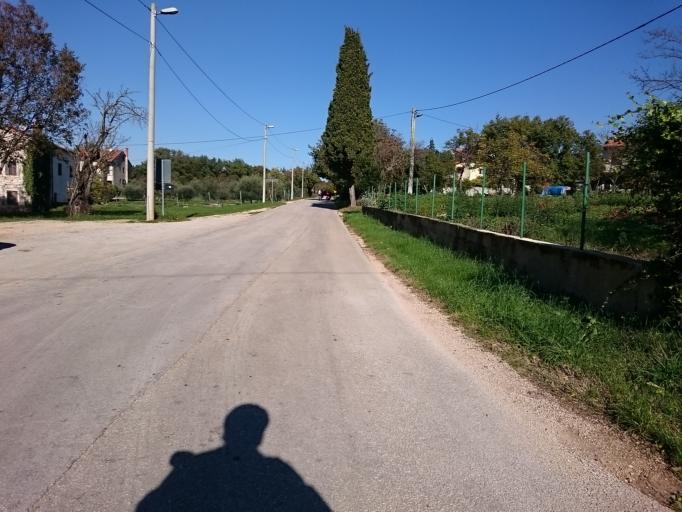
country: HR
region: Istarska
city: Umag
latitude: 45.4519
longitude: 13.5372
